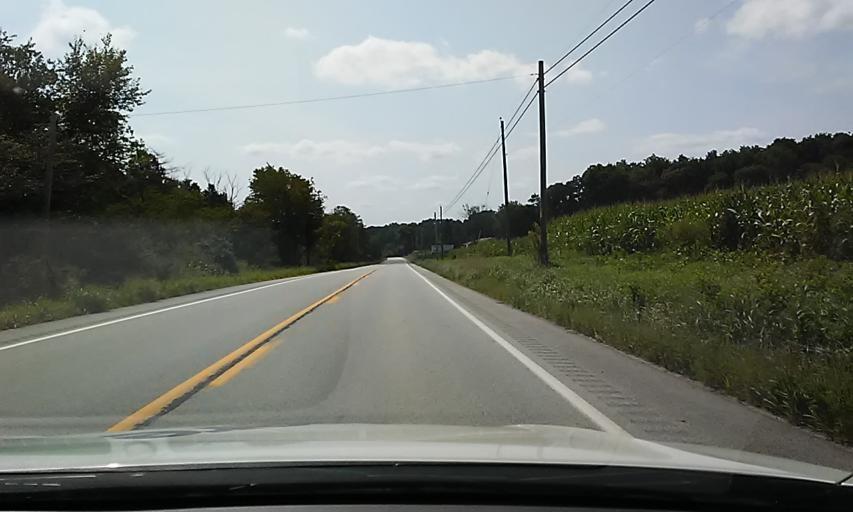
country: US
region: Pennsylvania
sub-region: Indiana County
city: Clymer
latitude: 40.7588
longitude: -79.0673
